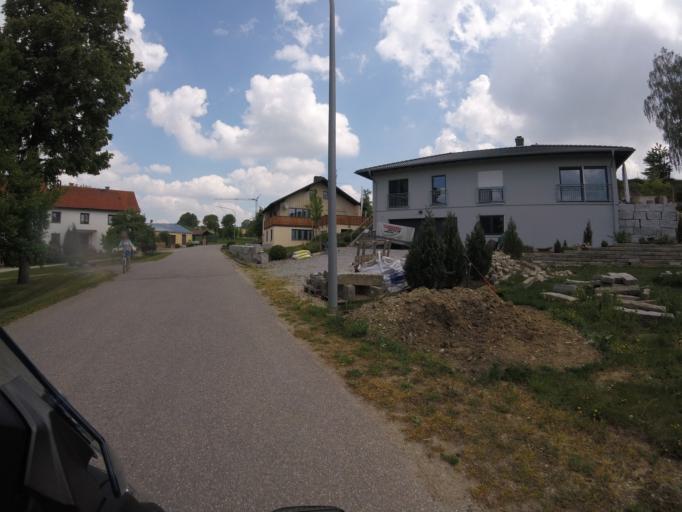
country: DE
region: Bavaria
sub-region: Lower Bavaria
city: Pfeffenhausen
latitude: 48.6689
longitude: 11.9060
